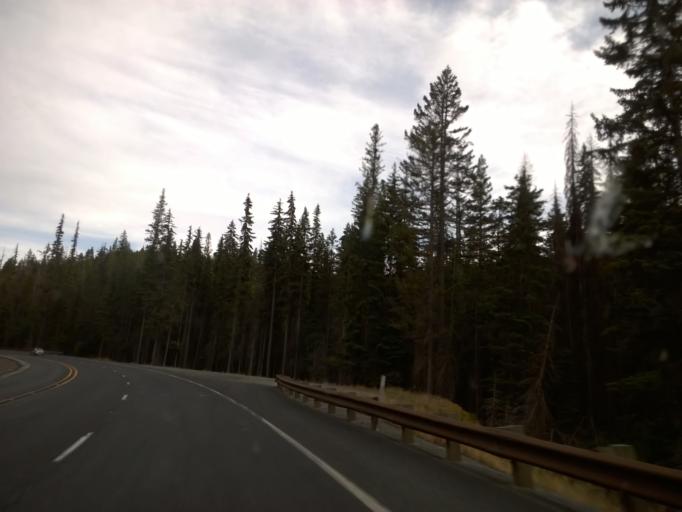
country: US
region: Washington
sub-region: Chelan County
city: Cashmere
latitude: 47.3486
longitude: -120.5711
